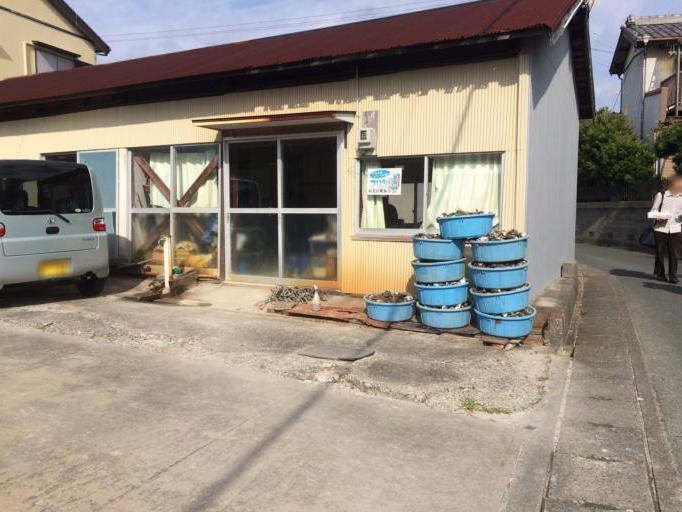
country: JP
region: Shizuoka
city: Kosai-shi
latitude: 34.6929
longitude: 137.5637
